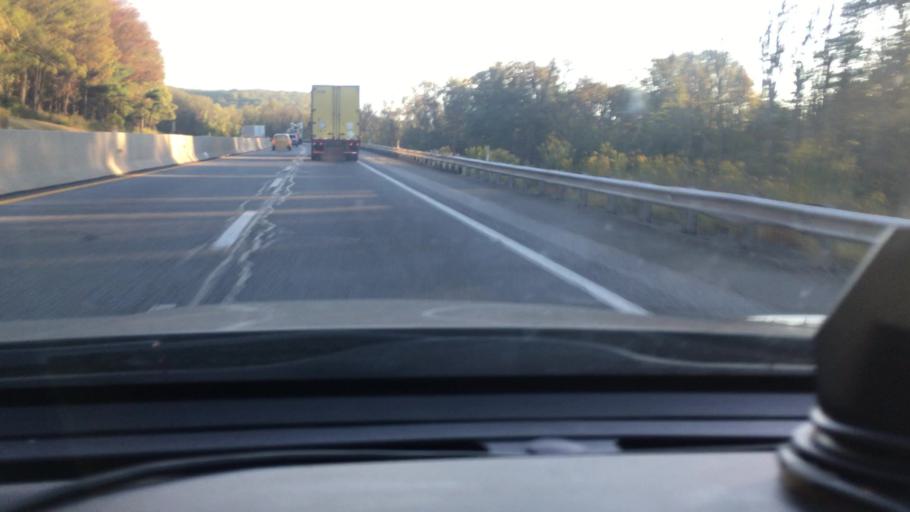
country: US
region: Pennsylvania
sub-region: Carbon County
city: Weissport East
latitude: 40.8922
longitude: -75.6427
